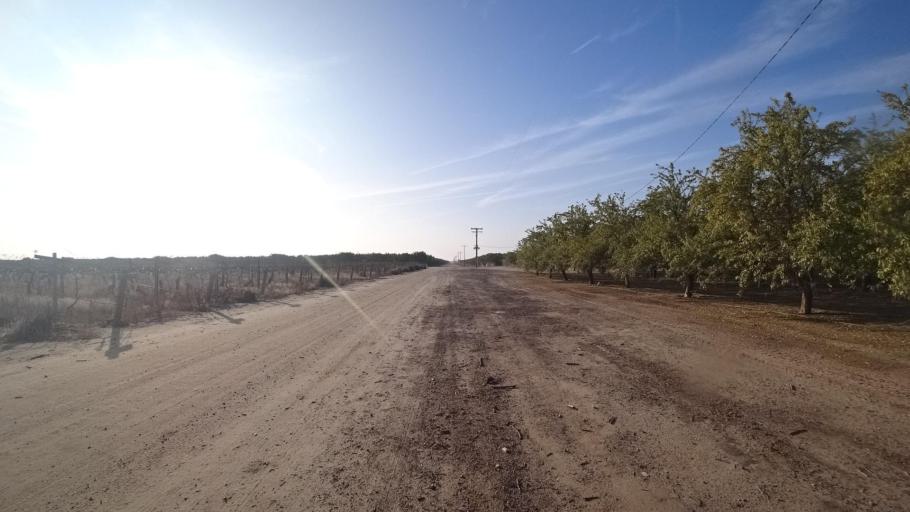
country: US
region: California
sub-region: Kern County
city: Delano
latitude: 35.7336
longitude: -119.1873
